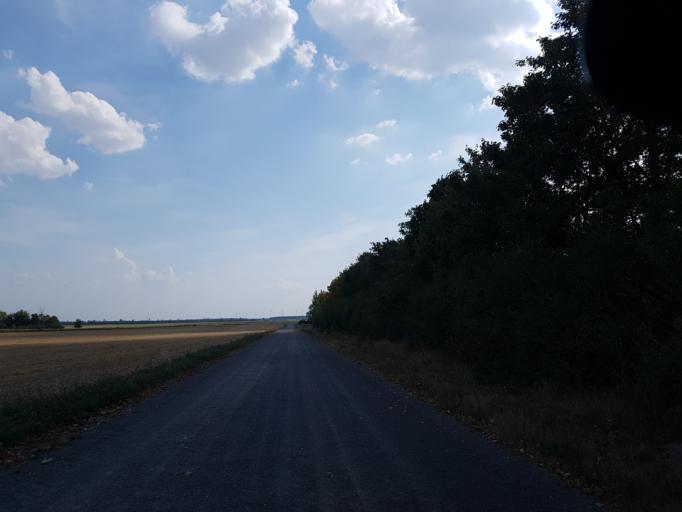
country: DE
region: Brandenburg
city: Treuenbrietzen
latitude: 51.9935
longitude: 12.8687
